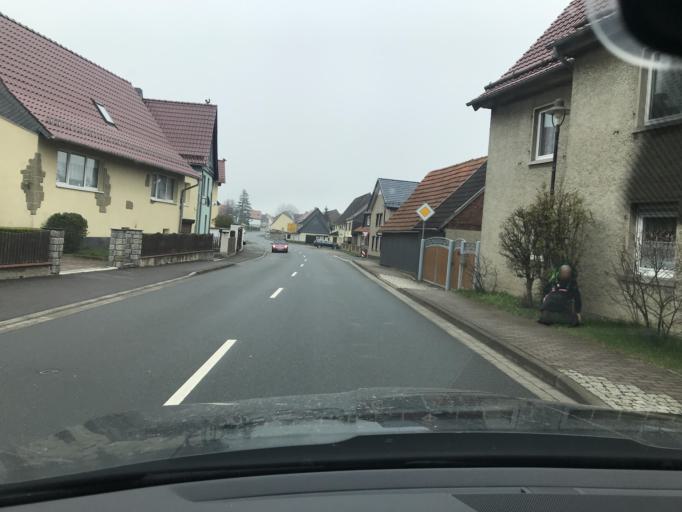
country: DE
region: Saxony-Anhalt
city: Harzgerode
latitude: 51.6028
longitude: 11.2003
